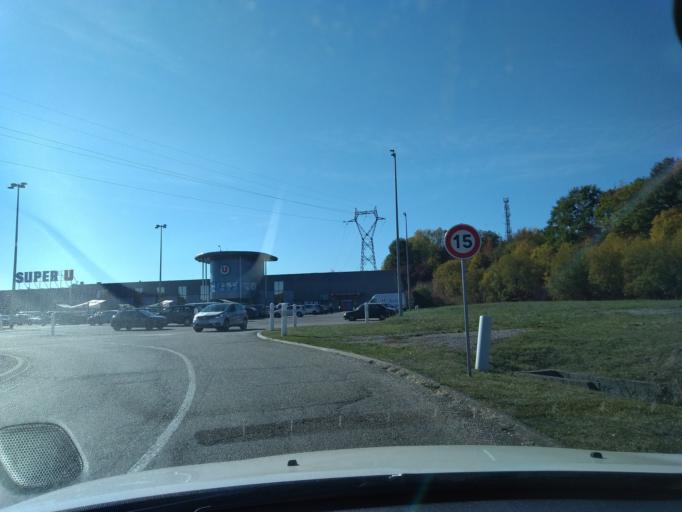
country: FR
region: Lorraine
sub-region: Departement de la Moselle
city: Neufgrange
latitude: 49.0876
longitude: 7.0392
